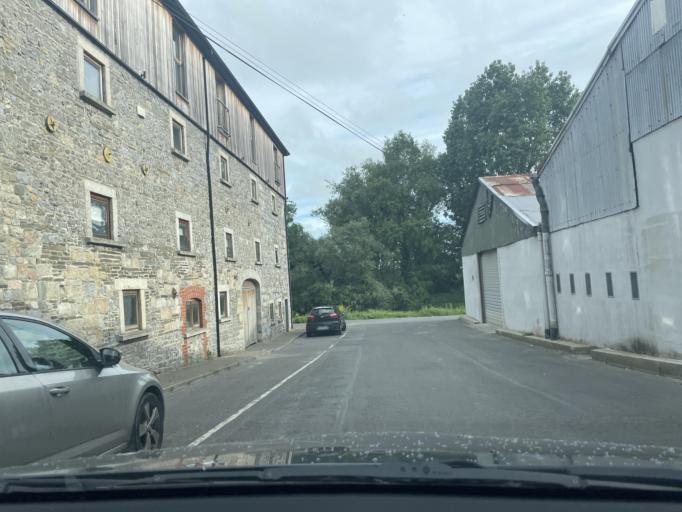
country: IE
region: Leinster
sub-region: County Carlow
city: Bagenalstown
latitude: 52.7030
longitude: -6.9617
